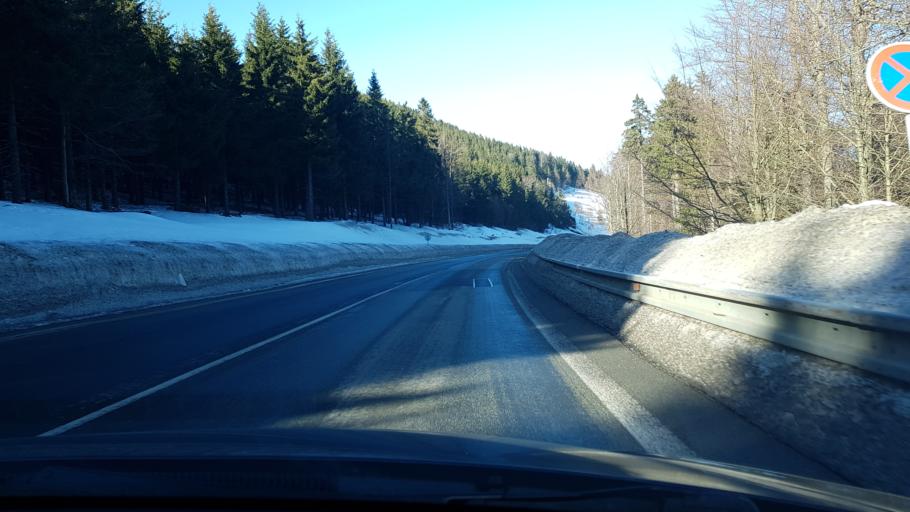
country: CZ
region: Olomoucky
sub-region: Okres Sumperk
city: Loucna nad Desnou
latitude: 50.1269
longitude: 17.1549
